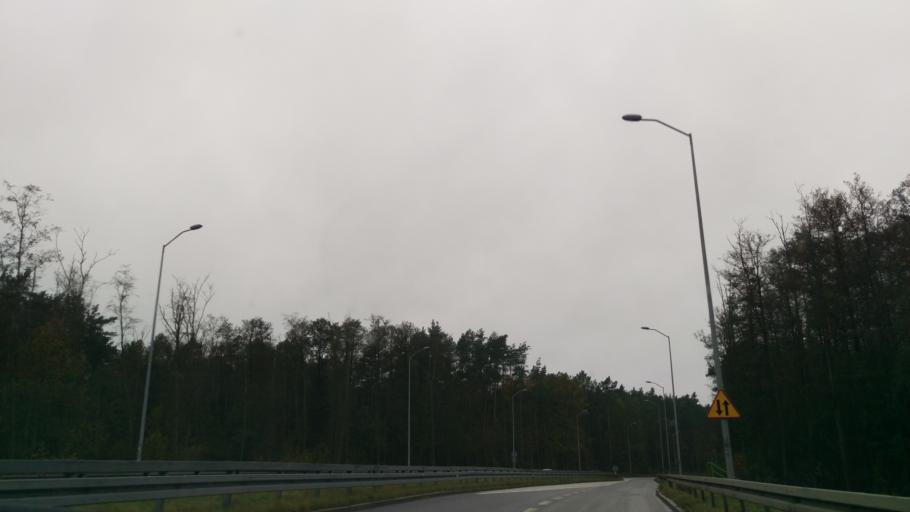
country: PL
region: West Pomeranian Voivodeship
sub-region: Powiat gryfinski
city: Stare Czarnowo
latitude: 53.3964
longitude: 14.7123
